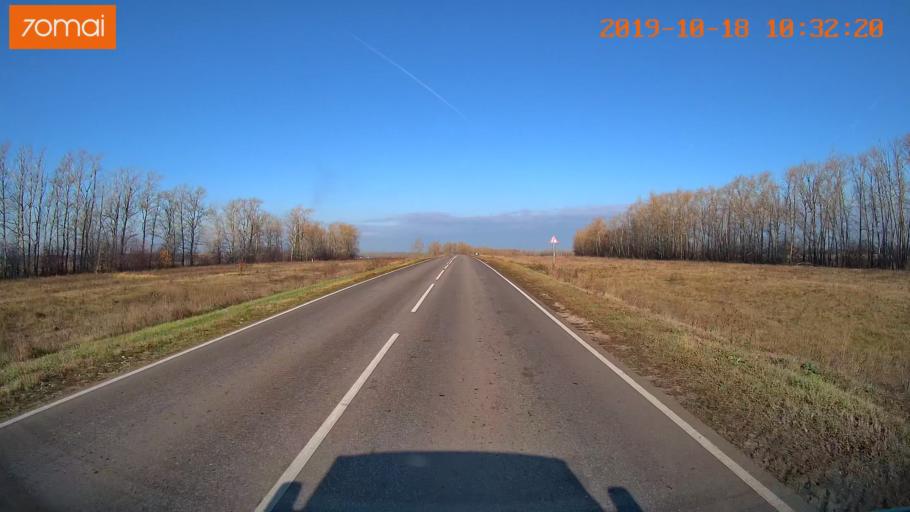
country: RU
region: Tula
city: Kurkino
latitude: 53.4927
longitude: 38.6239
